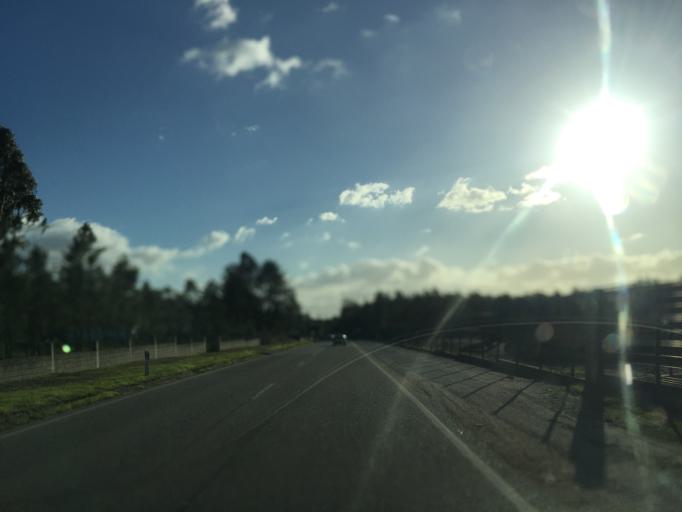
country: PT
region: Leiria
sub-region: Leiria
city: Monte Redondo
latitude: 39.9239
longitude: -8.8084
